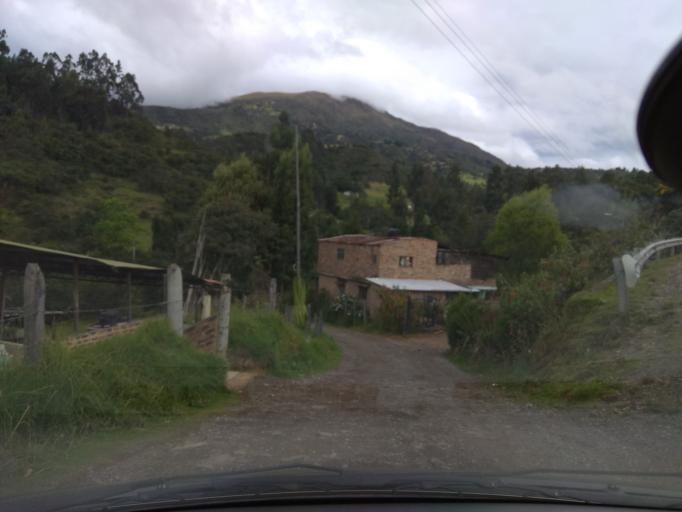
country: CO
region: Boyaca
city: Santa Rosa de Viterbo
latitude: 5.9012
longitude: -72.9761
